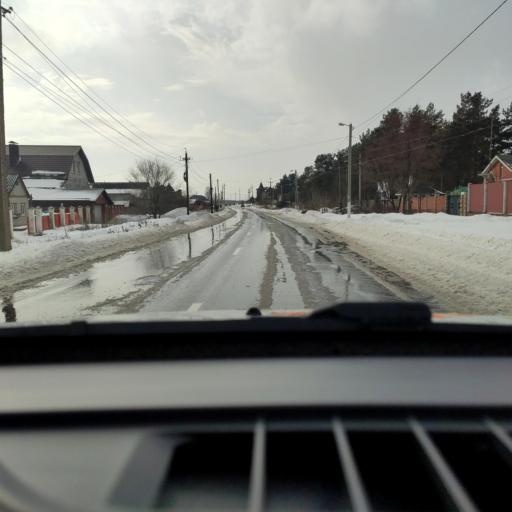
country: RU
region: Voronezj
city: Podgornoye
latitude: 51.7776
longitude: 39.1298
